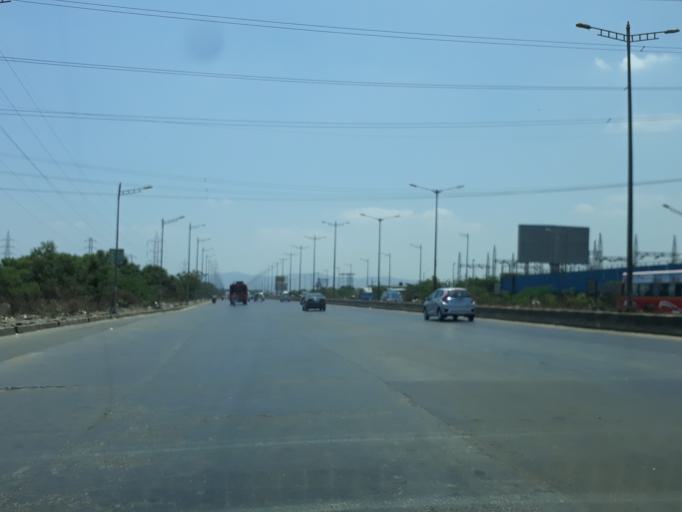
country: IN
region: Maharashtra
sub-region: Mumbai Suburban
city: Mumbai
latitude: 19.0526
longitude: 72.9402
